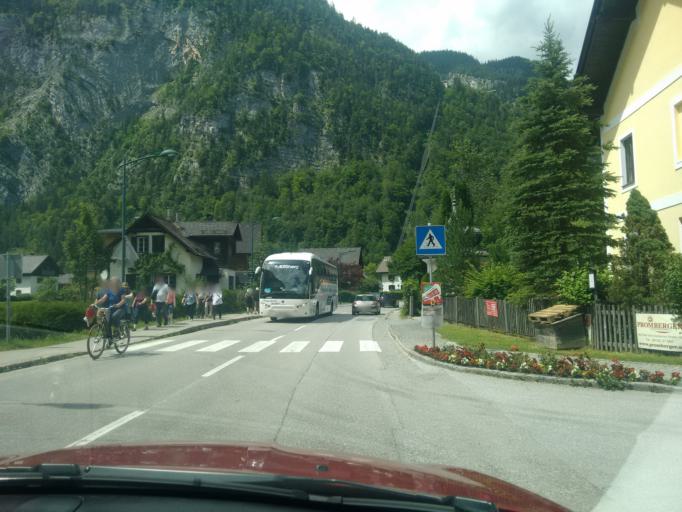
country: AT
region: Upper Austria
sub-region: Politischer Bezirk Gmunden
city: Bad Goisern
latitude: 47.5533
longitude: 13.6480
